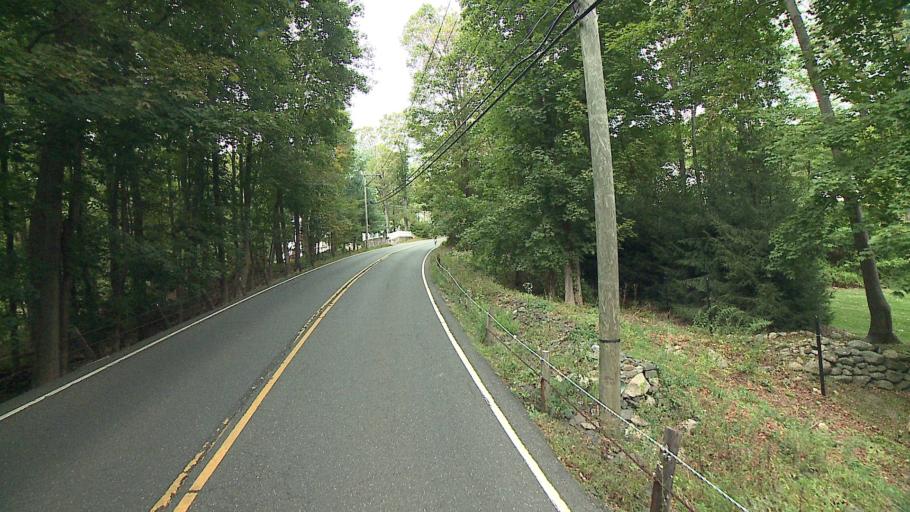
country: US
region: Connecticut
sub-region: Fairfield County
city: Ridgefield
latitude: 41.2507
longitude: -73.4902
